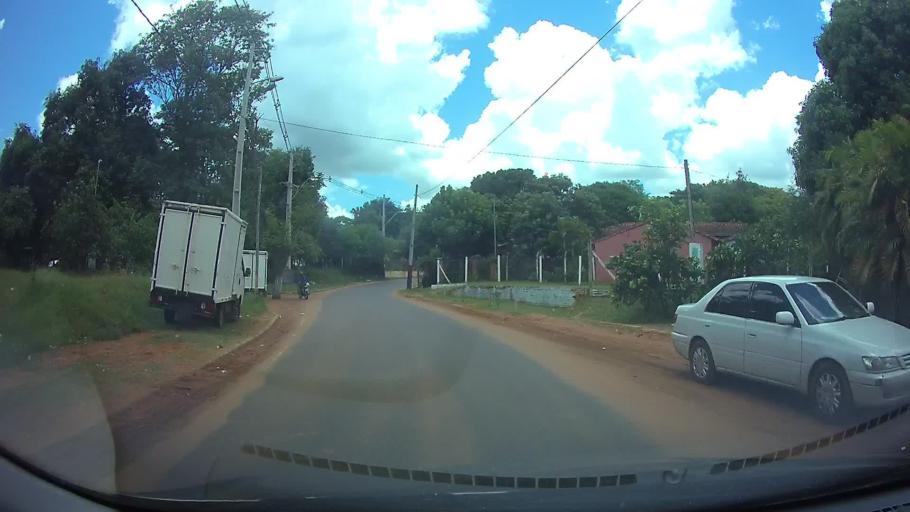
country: PY
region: Central
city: Capiata
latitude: -25.3020
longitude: -57.4417
